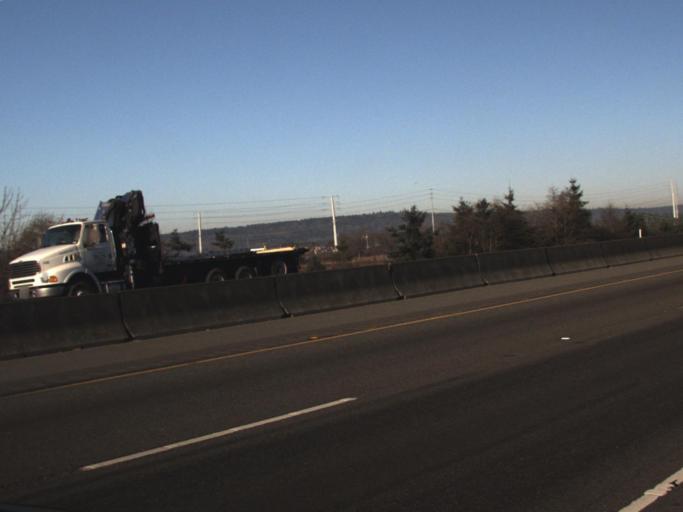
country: US
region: Washington
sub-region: Snohomish County
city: Marysville
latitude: 48.0313
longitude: -122.1771
